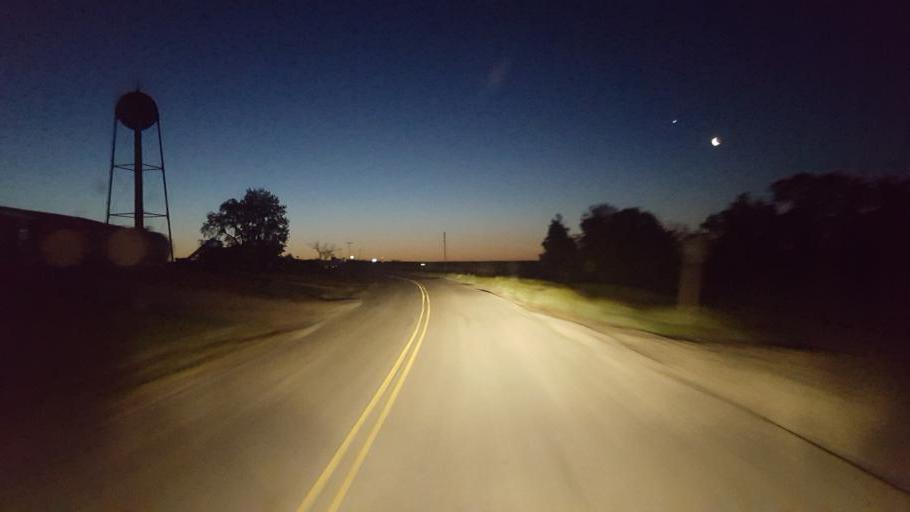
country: US
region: Missouri
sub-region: Mercer County
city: Princeton
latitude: 40.4386
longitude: -93.7662
